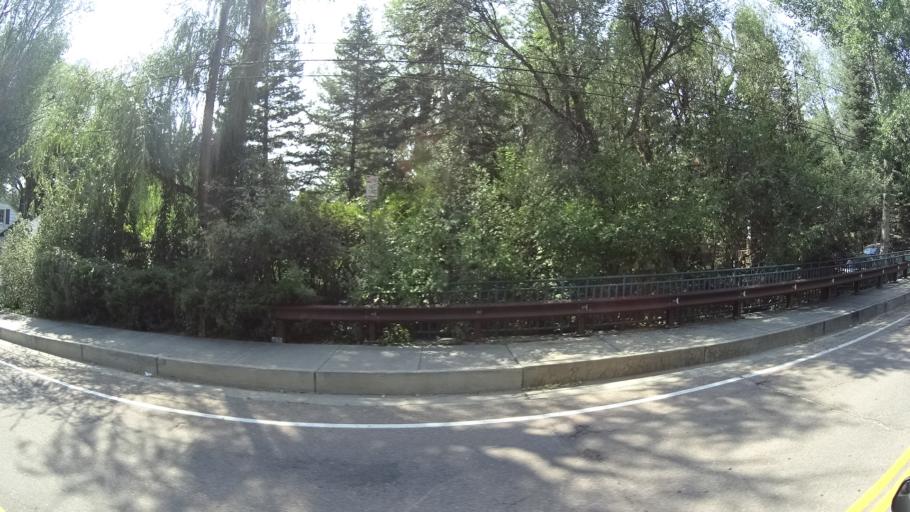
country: US
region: Colorado
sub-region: El Paso County
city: Colorado Springs
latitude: 38.8027
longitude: -104.8342
